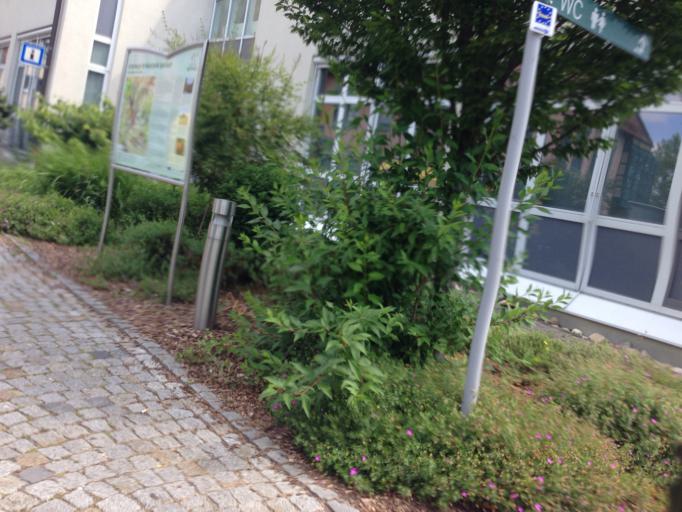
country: DE
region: Bavaria
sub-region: Regierungsbezirk Unterfranken
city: Schollkrippen
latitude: 50.0847
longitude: 9.2459
